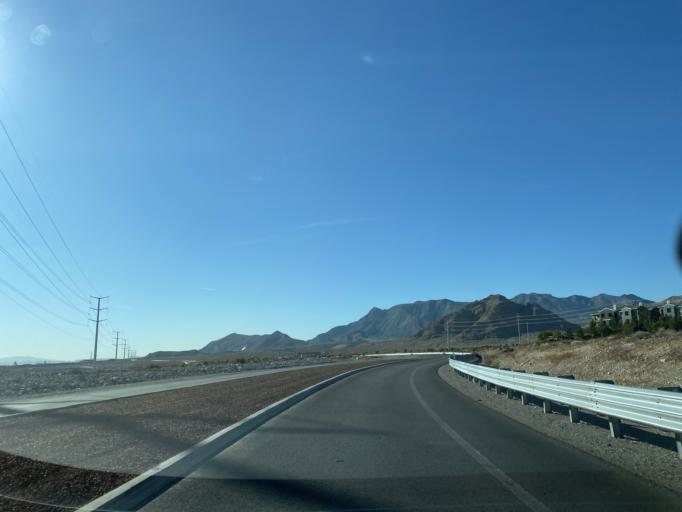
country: US
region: Nevada
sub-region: Clark County
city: Summerlin South
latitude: 36.2755
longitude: -115.3290
